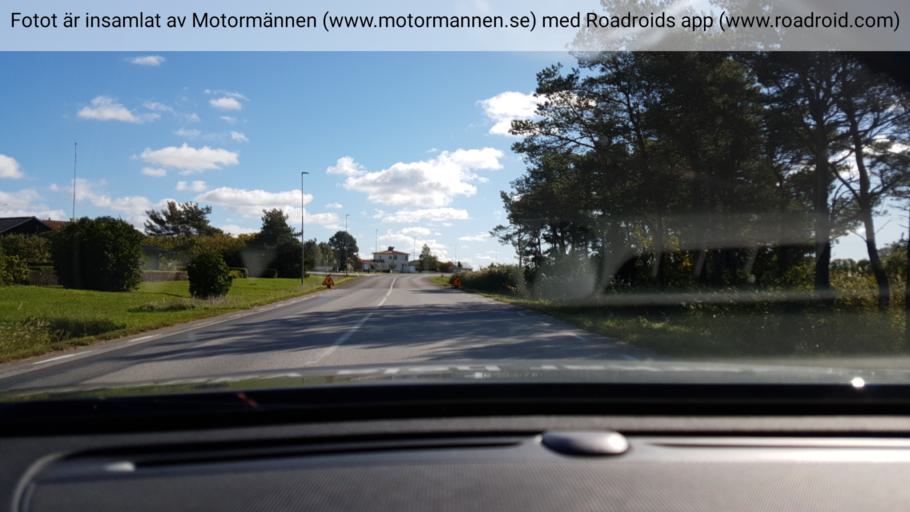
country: SE
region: Gotland
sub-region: Gotland
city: Slite
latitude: 57.6978
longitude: 18.7960
